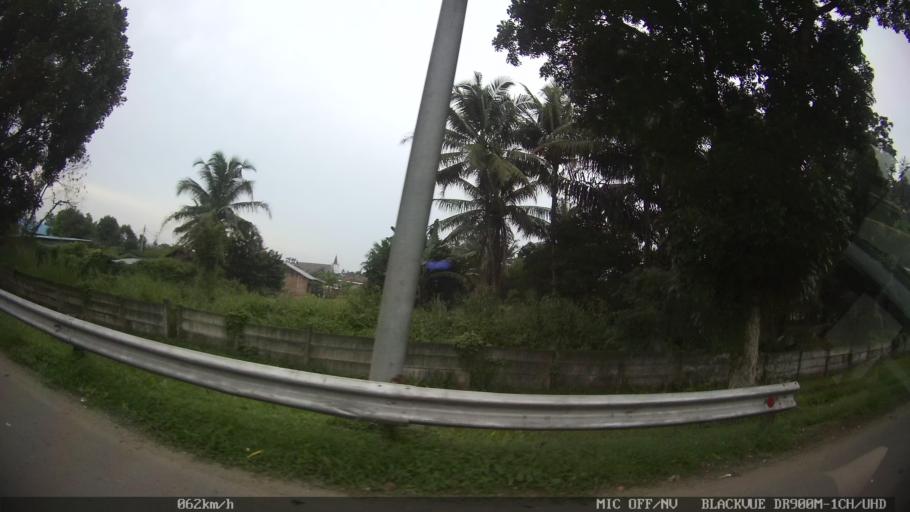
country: ID
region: North Sumatra
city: Deli Tua
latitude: 3.5513
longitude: 98.7251
